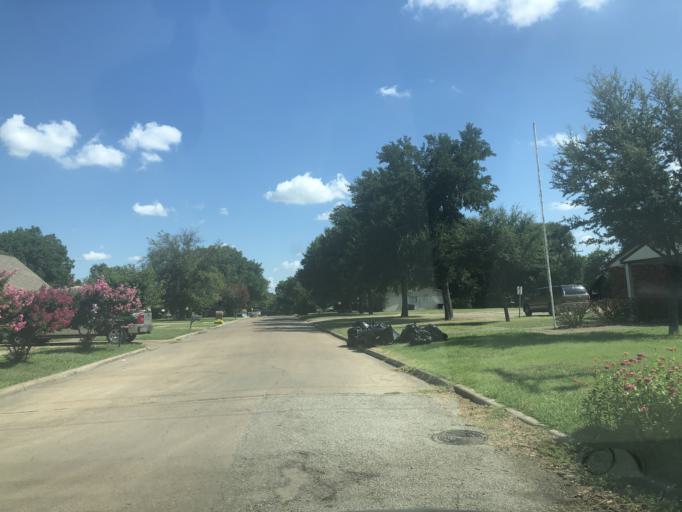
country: US
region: Texas
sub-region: Dallas County
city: Grand Prairie
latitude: 32.7335
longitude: -97.0049
